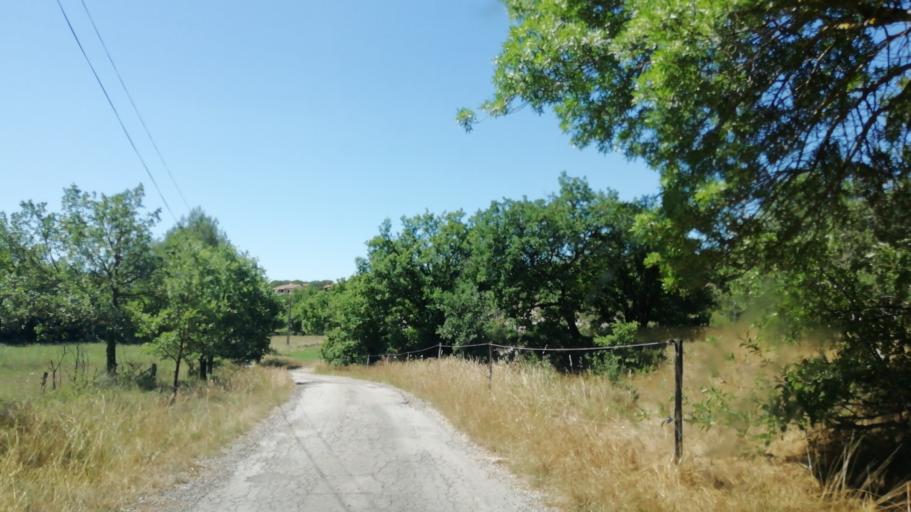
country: FR
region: Languedoc-Roussillon
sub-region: Departement de l'Herault
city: Saint-Martin-de-Londres
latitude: 43.8308
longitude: 3.7767
